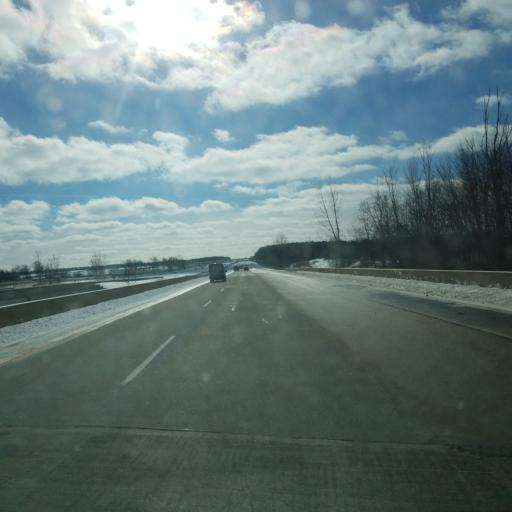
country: US
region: Michigan
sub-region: Clinton County
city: DeWitt
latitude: 42.8551
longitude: -84.5190
